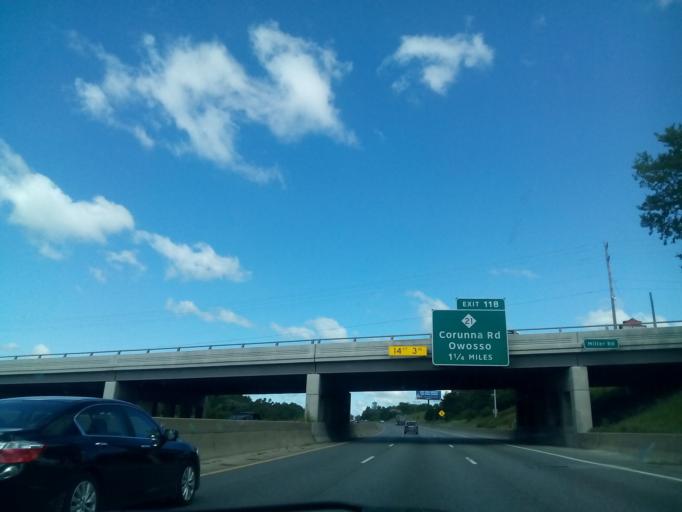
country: US
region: Michigan
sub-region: Genesee County
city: Flint
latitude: 42.9895
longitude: -83.7382
